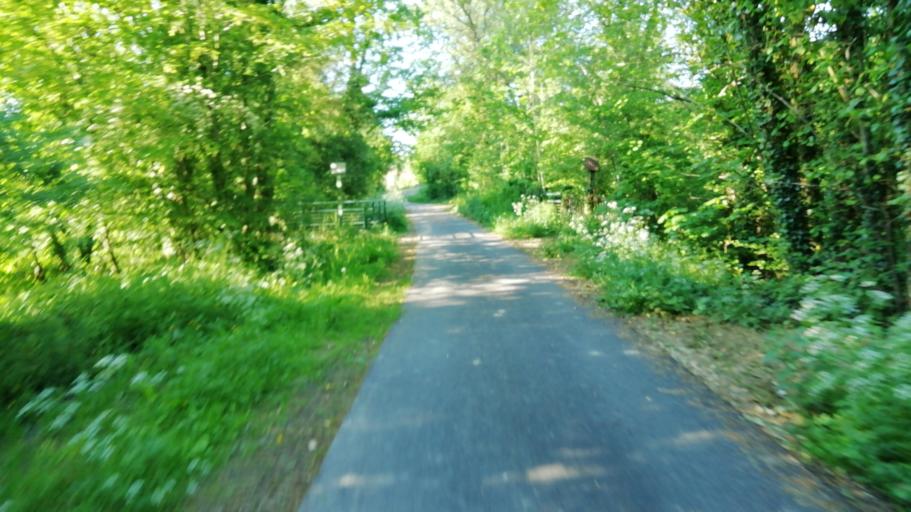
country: FR
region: Nord-Pas-de-Calais
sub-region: Departement du Nord
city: Ferriere-la-Grande
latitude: 50.2070
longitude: 4.0336
